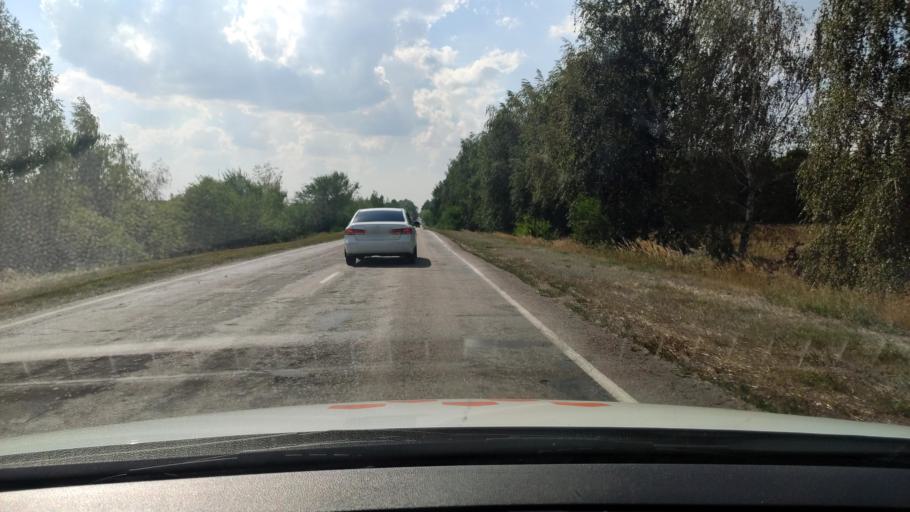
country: RU
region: Voronezj
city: Ertil'
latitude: 51.7844
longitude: 40.5724
